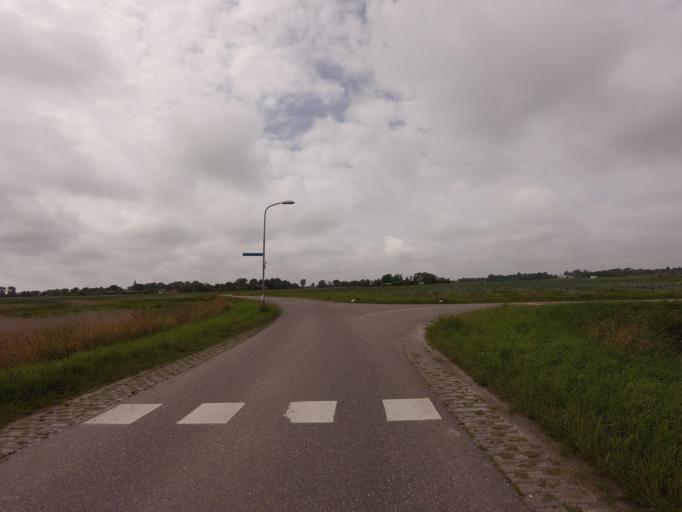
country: NL
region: North Holland
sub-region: Gemeente Schagen
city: Schagen
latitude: 52.7736
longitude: 4.7800
